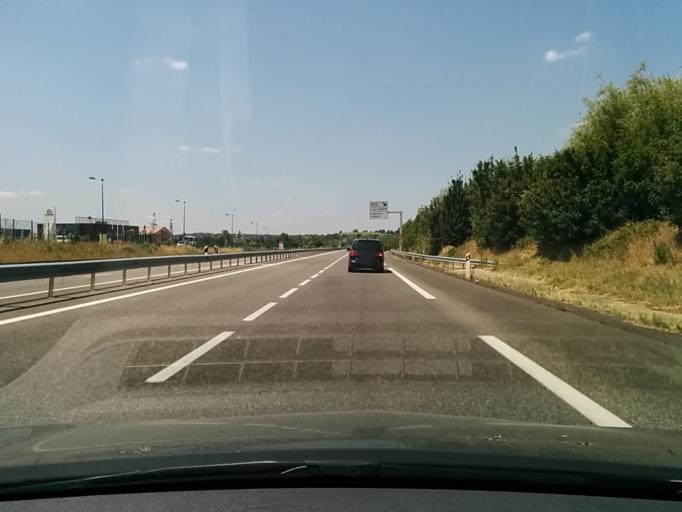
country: FR
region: Midi-Pyrenees
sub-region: Departement du Gers
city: Pujaudran
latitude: 43.6056
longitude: 1.0756
